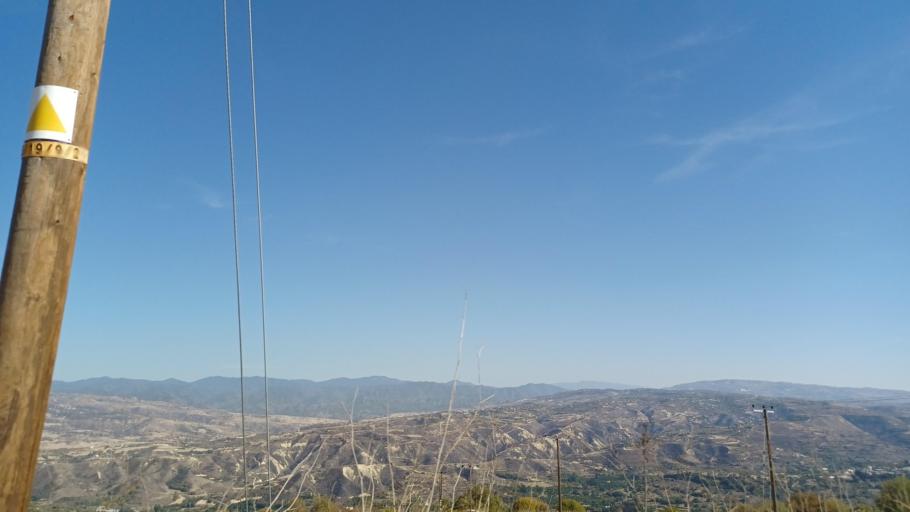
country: CY
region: Pafos
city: Pegeia
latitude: 34.9329
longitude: 32.4493
